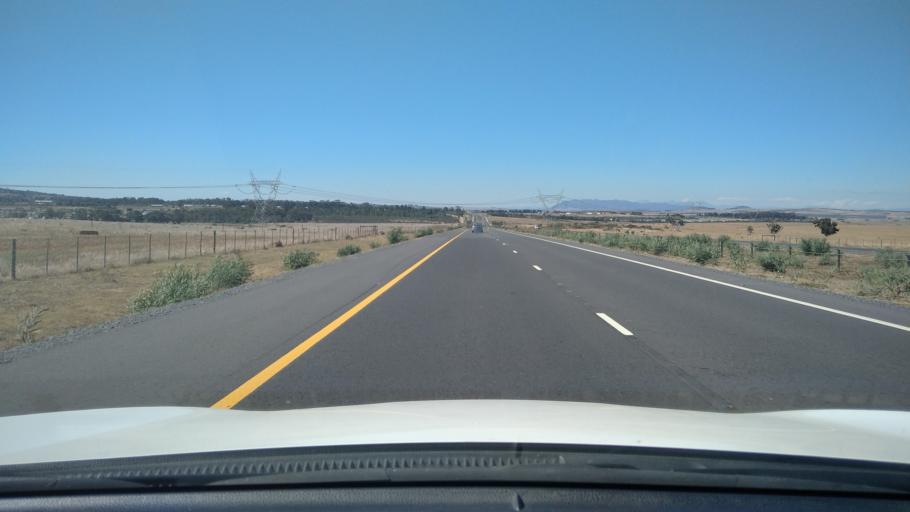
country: ZA
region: Western Cape
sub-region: City of Cape Town
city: Atlantis
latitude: -33.6295
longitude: 18.5815
